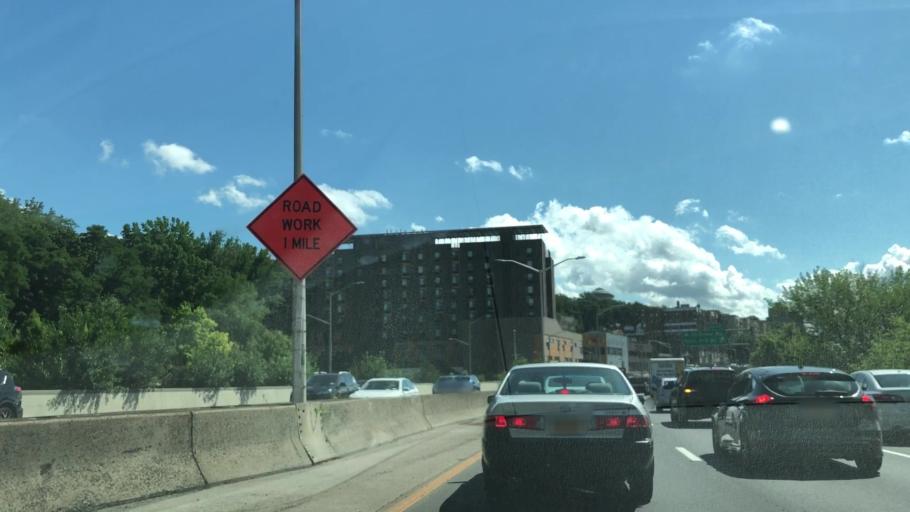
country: US
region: New York
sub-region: New York County
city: Inwood
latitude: 40.8645
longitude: -73.9102
